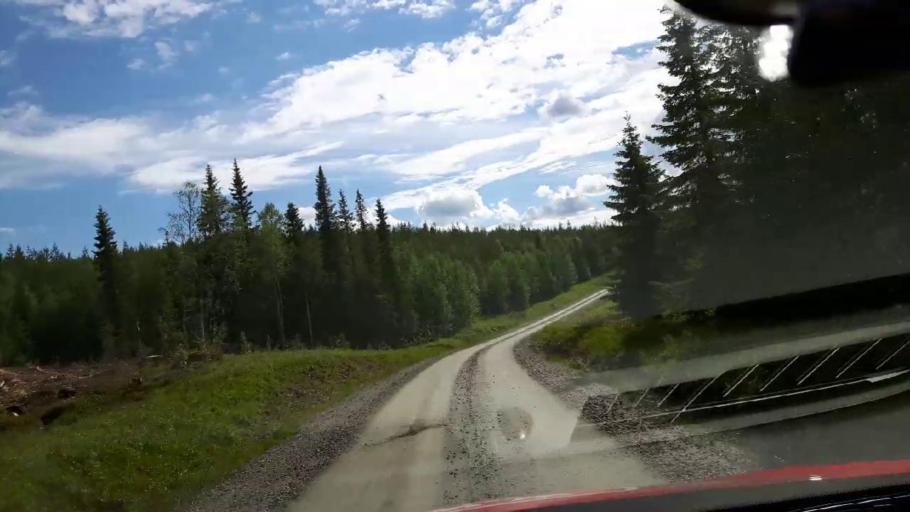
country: SE
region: Jaemtland
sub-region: Krokoms Kommun
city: Valla
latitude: 63.8944
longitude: 14.1724
